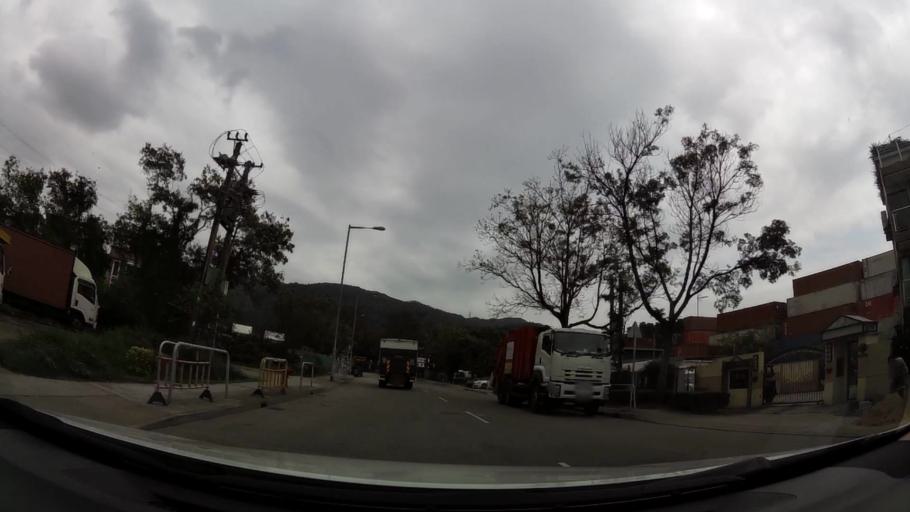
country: HK
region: Tuen Mun
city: Tuen Mun
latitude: 22.4241
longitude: 113.9917
